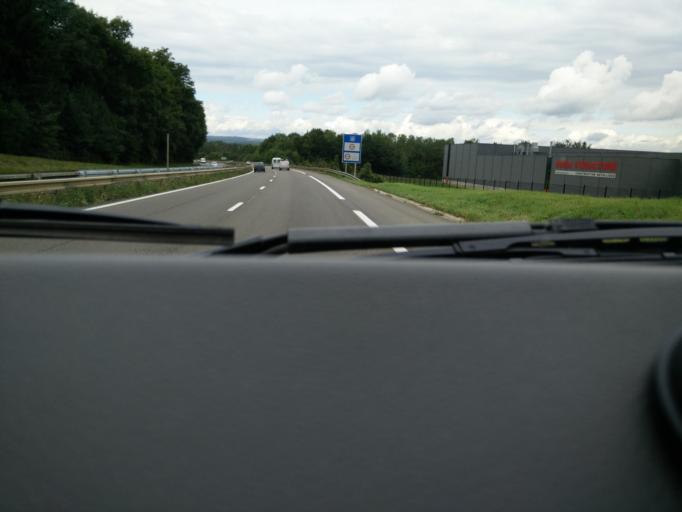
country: FR
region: Champagne-Ardenne
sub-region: Departement des Ardennes
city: Donchery
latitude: 49.7013
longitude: 4.9039
